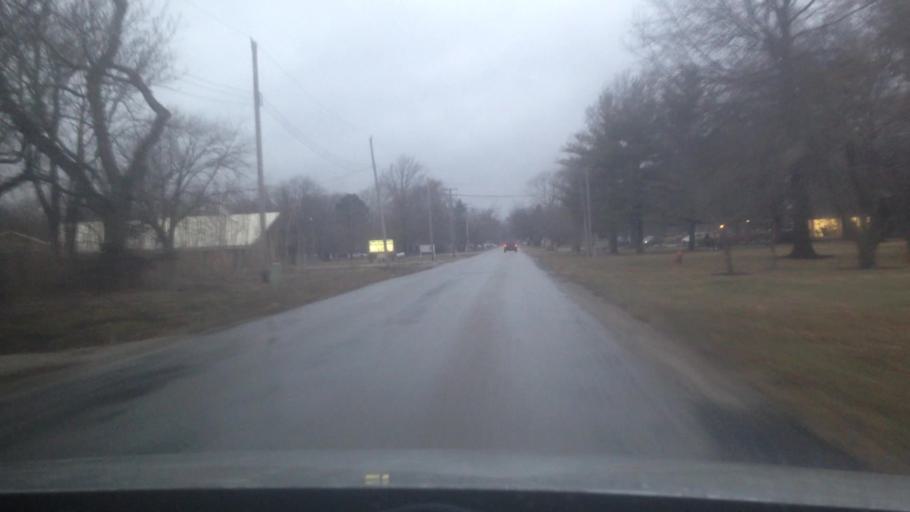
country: US
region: Illinois
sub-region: Christian County
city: Pana
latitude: 39.3830
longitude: -89.0655
